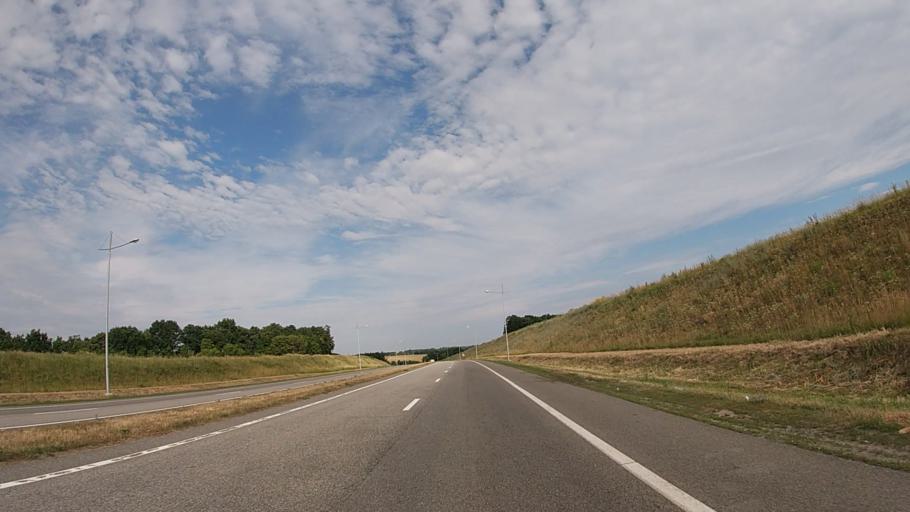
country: RU
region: Belgorod
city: Tomarovka
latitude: 50.7062
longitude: 36.2146
